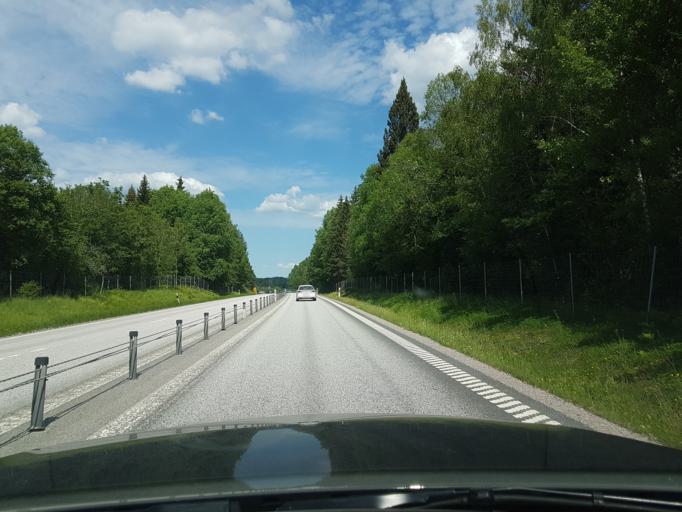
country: SE
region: Stockholm
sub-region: Osterakers Kommun
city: Akersberga
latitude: 59.5519
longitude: 18.2289
